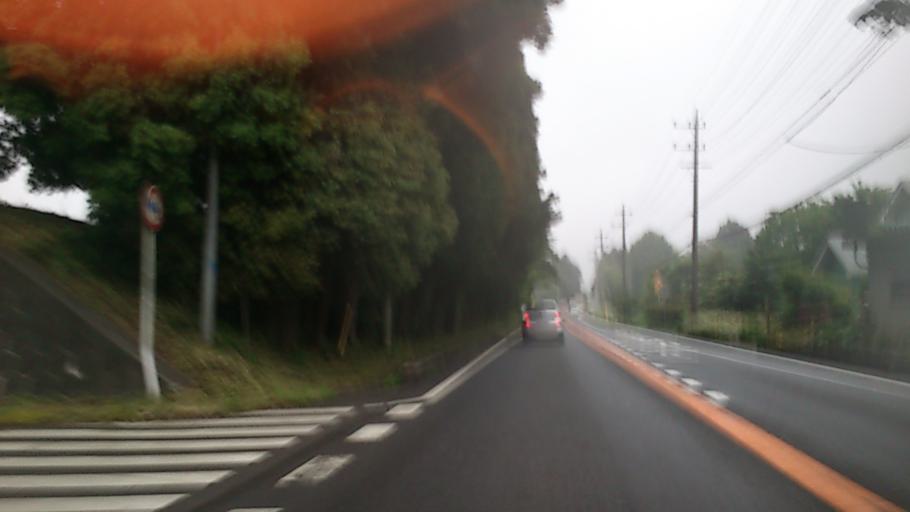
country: JP
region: Tochigi
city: Kuroiso
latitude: 37.0507
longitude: 140.1049
